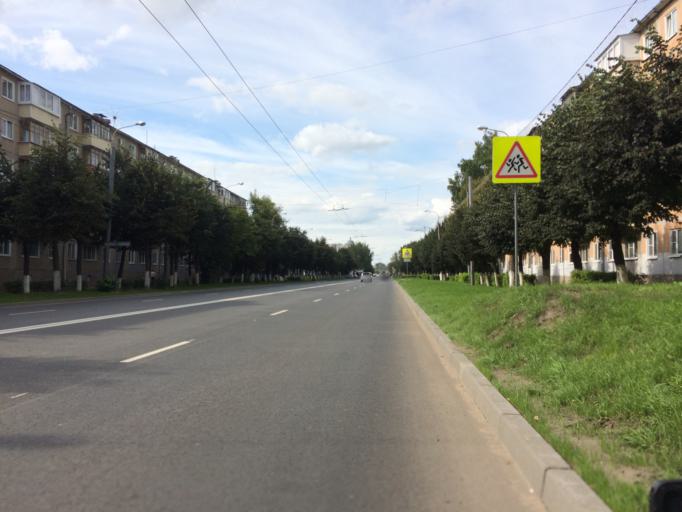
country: RU
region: Mariy-El
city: Yoshkar-Ola
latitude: 56.6348
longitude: 47.8767
